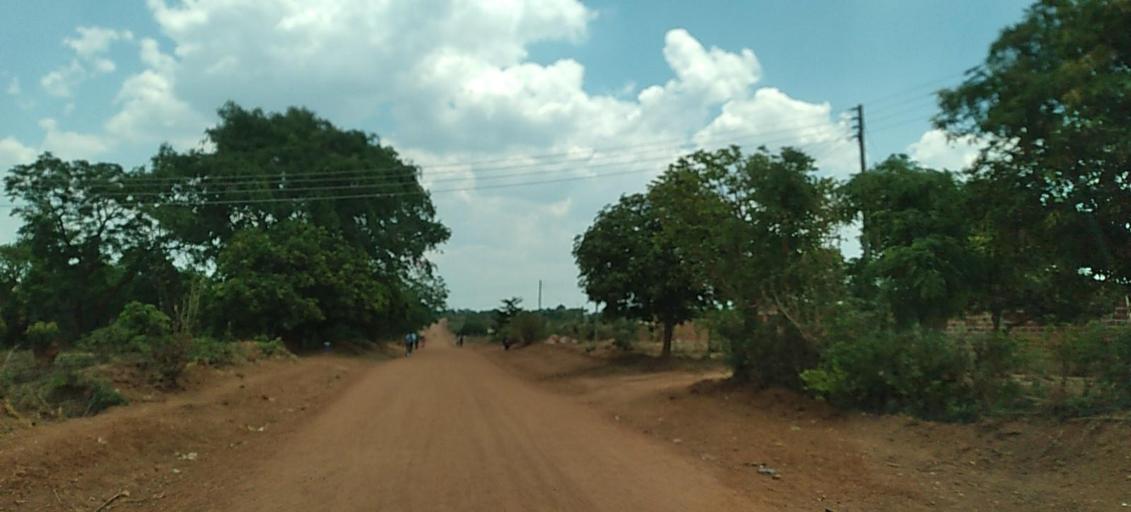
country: ZM
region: Copperbelt
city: Luanshya
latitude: -13.3627
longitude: 28.4128
